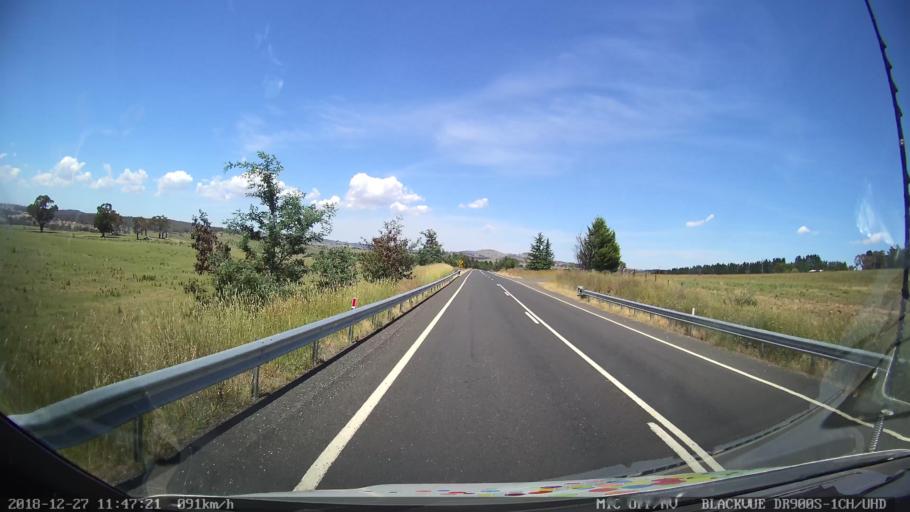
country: AU
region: New South Wales
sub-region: Bathurst Regional
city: Perthville
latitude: -33.5954
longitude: 149.4462
